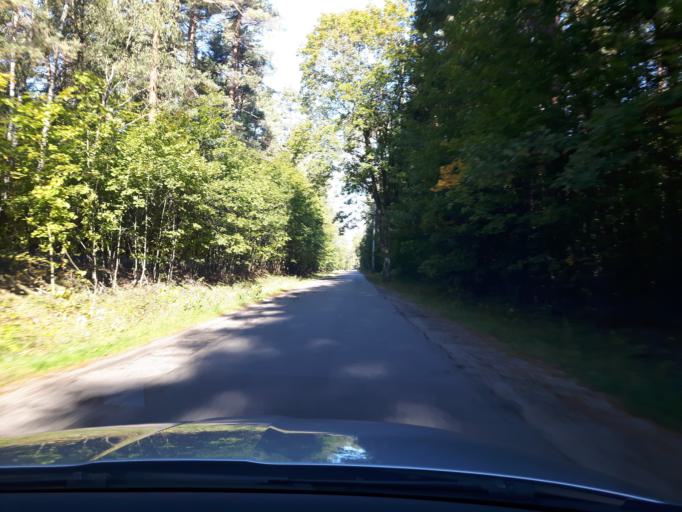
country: PL
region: Warmian-Masurian Voivodeship
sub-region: Powiat olsztynski
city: Gietrzwald
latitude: 53.6968
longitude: 20.2315
